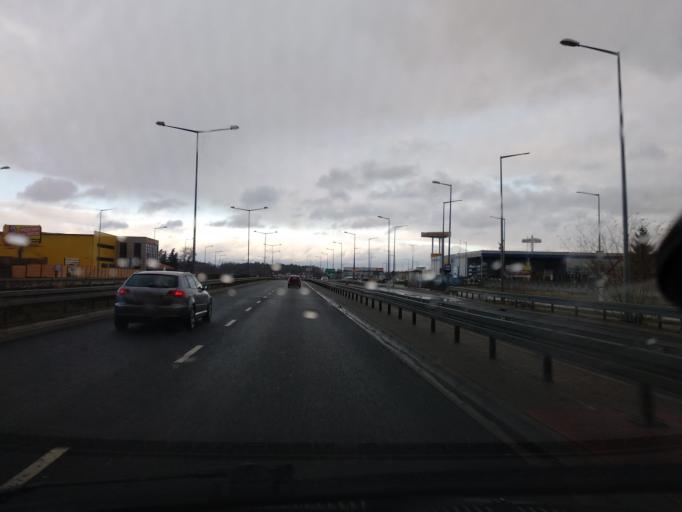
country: PL
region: Greater Poland Voivodeship
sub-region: Powiat koninski
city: Stare Miasto
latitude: 52.1838
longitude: 18.2264
